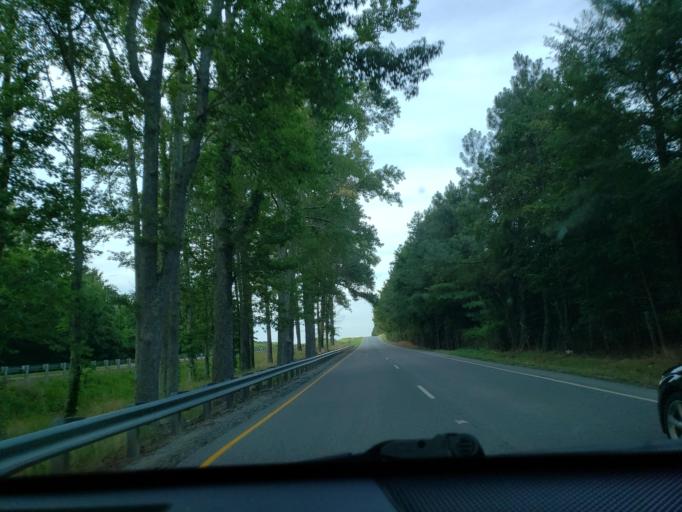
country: US
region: Virginia
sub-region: Brunswick County
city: Lawrenceville
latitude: 36.7314
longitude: -77.9098
